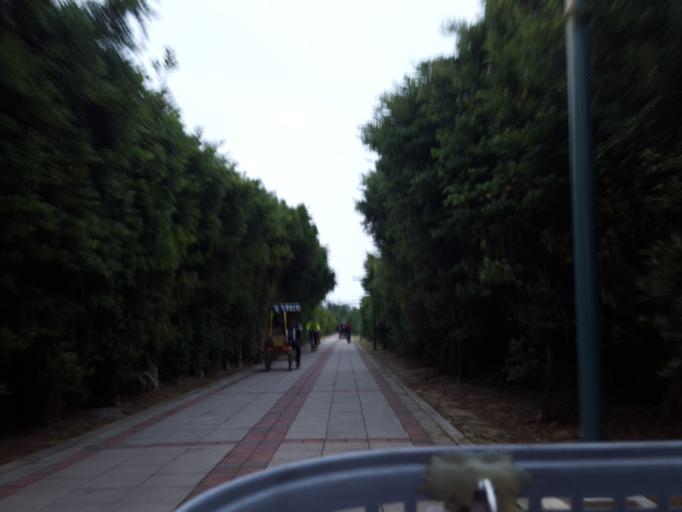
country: TW
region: Taiwan
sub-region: Hsinchu
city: Hsinchu
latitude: 24.8410
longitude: 120.9209
